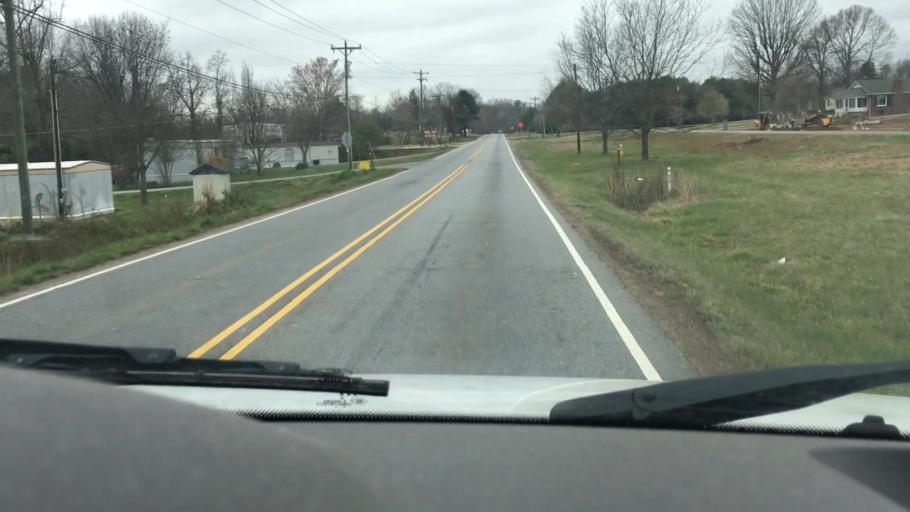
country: US
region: North Carolina
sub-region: Iredell County
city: Troutman
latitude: 35.6896
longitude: -80.8674
